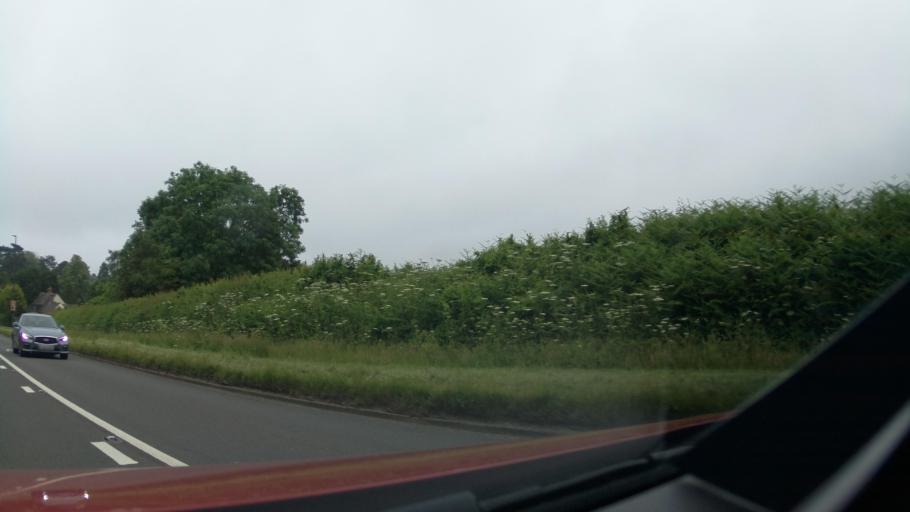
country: GB
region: England
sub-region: Derbyshire
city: Netherseal
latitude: 52.7271
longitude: -1.5605
